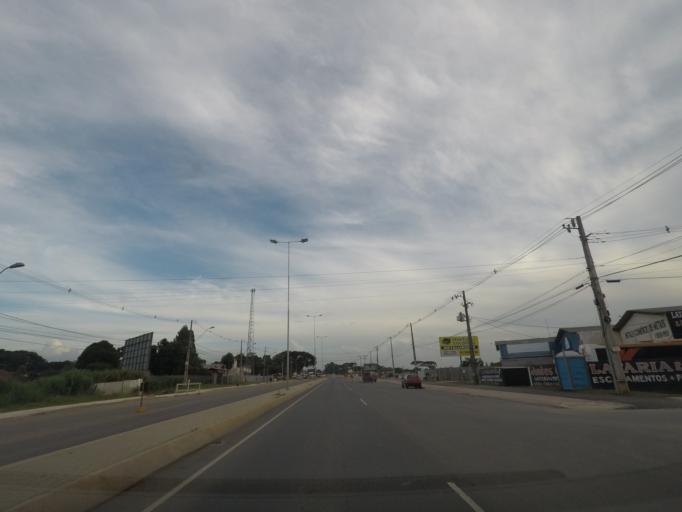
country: BR
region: Parana
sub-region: Colombo
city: Colombo
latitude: -25.3233
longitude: -49.2203
